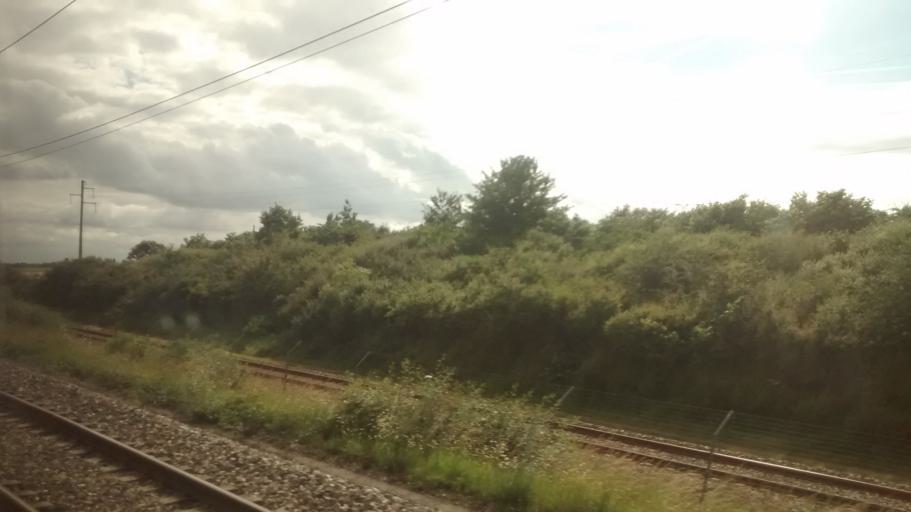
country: FR
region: Centre
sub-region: Departement d'Eure-et-Loir
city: Beville-le-Comte
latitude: 48.4189
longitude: 1.7563
